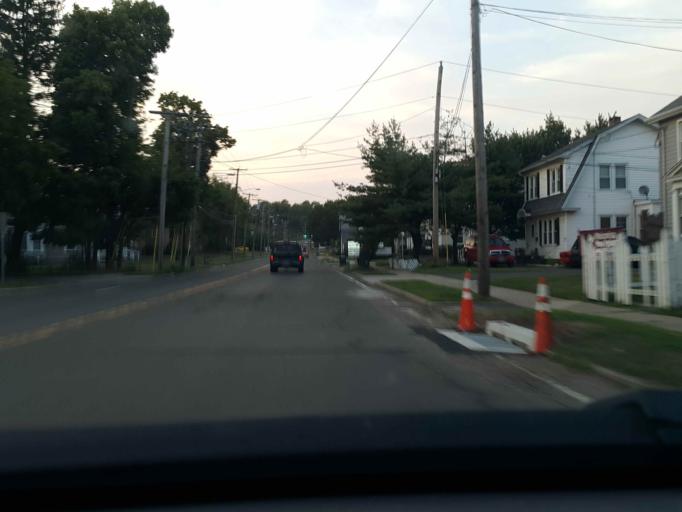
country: US
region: Connecticut
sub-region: New Haven County
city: East Haven
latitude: 41.2789
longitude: -72.8718
